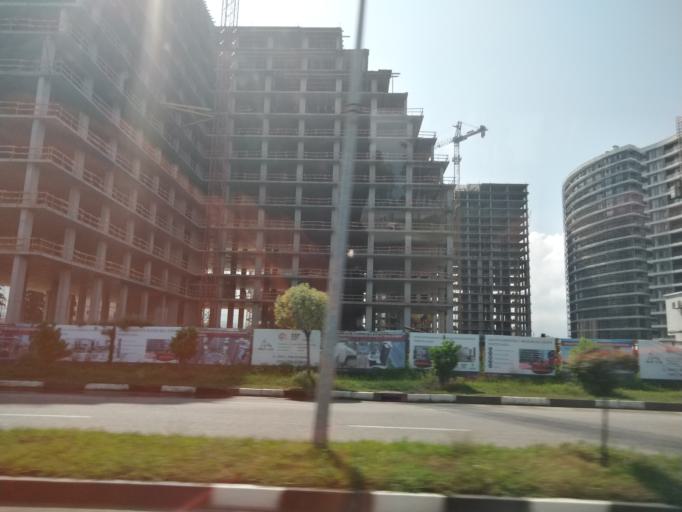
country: GE
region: Ajaria
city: Batumi
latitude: 41.6249
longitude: 41.5973
